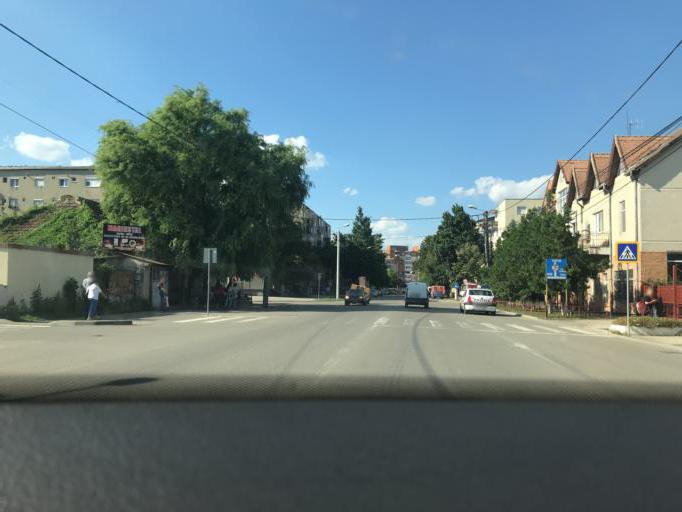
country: RO
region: Bihor
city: Margita
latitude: 47.3408
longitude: 22.3310
